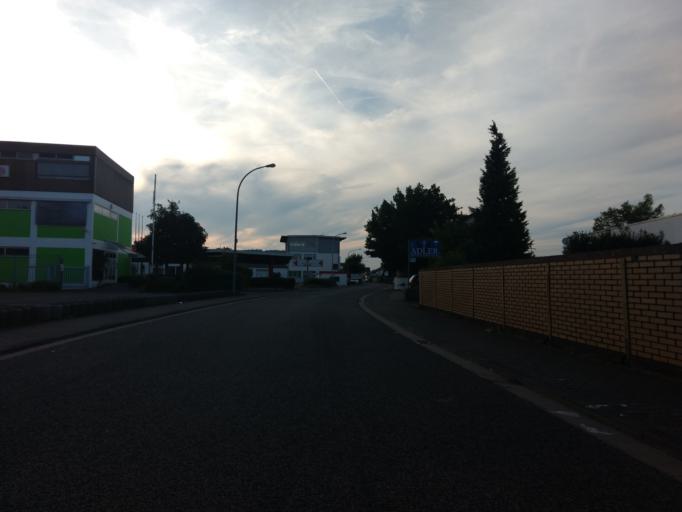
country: DE
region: Saarland
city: Saarlouis
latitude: 49.3117
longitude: 6.7369
